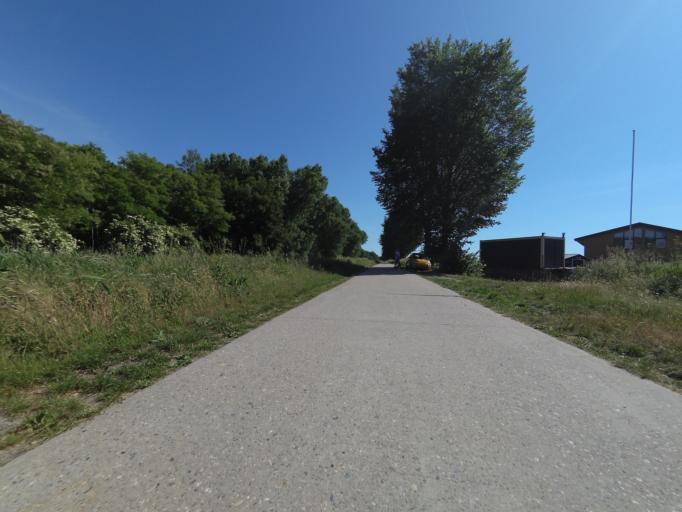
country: NL
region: North Holland
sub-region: Gemeente Huizen
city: Huizen
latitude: 52.3256
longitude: 5.3186
